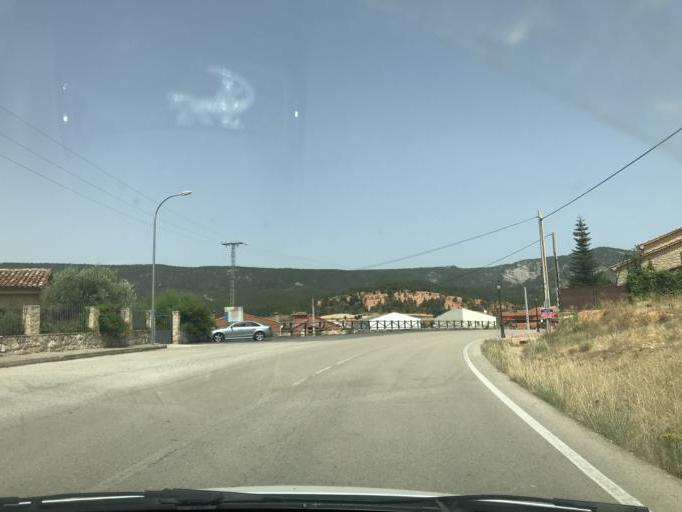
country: ES
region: Castille-La Mancha
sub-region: Provincia de Cuenca
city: Canamares
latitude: 40.4487
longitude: -2.2384
